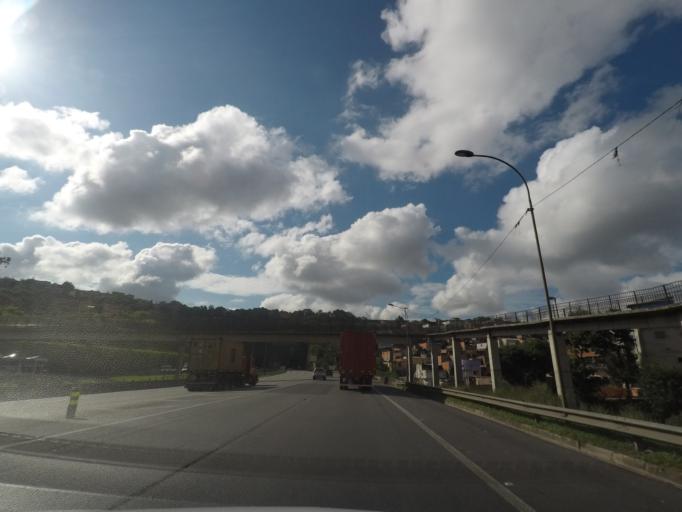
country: BR
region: Sao Paulo
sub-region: Embu
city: Embu
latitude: -23.6287
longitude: -46.8295
